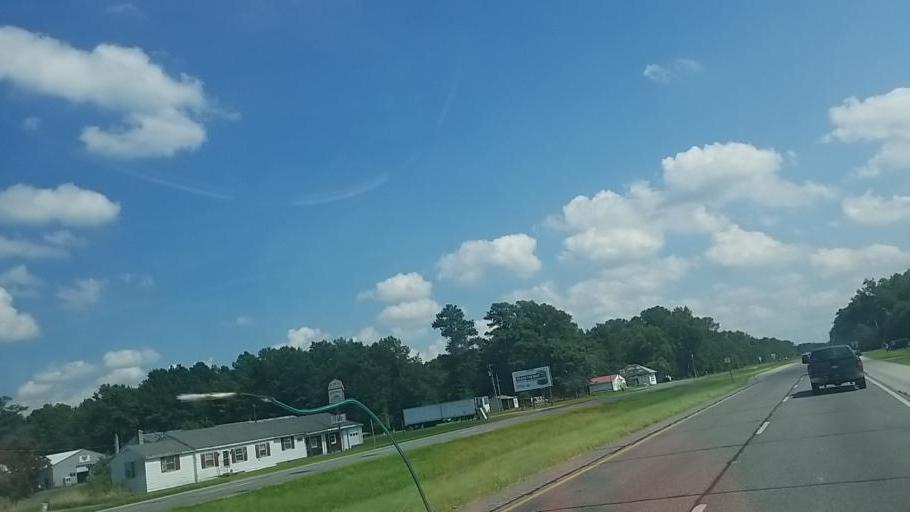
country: US
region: Delaware
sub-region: Sussex County
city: Georgetown
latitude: 38.7362
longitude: -75.4218
